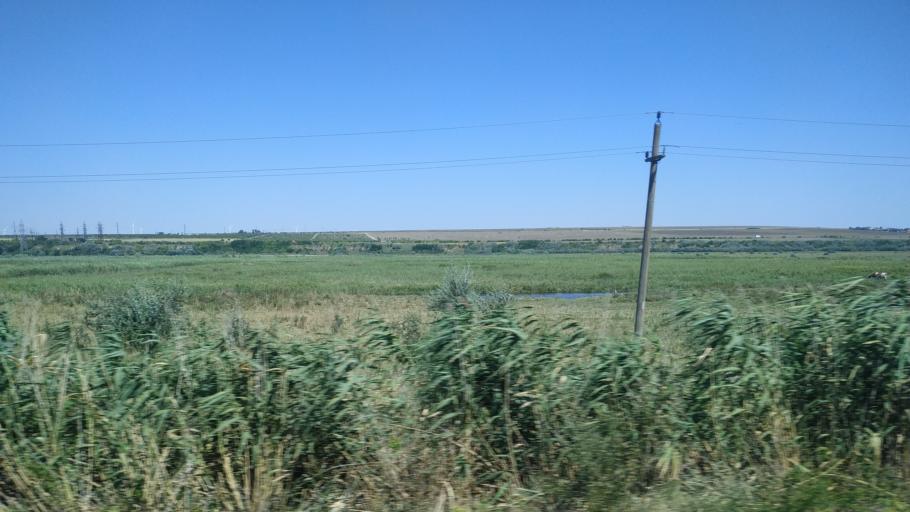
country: RO
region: Constanta
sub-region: Comuna Mircea Voda
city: Satu Nou
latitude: 44.2613
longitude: 28.2025
